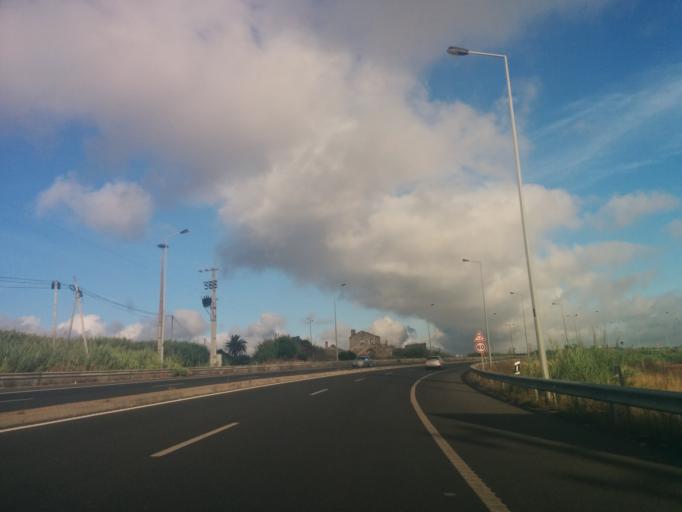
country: PT
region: Leiria
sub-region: Peniche
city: Atouguia da Baleia
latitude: 39.3470
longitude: -9.3438
